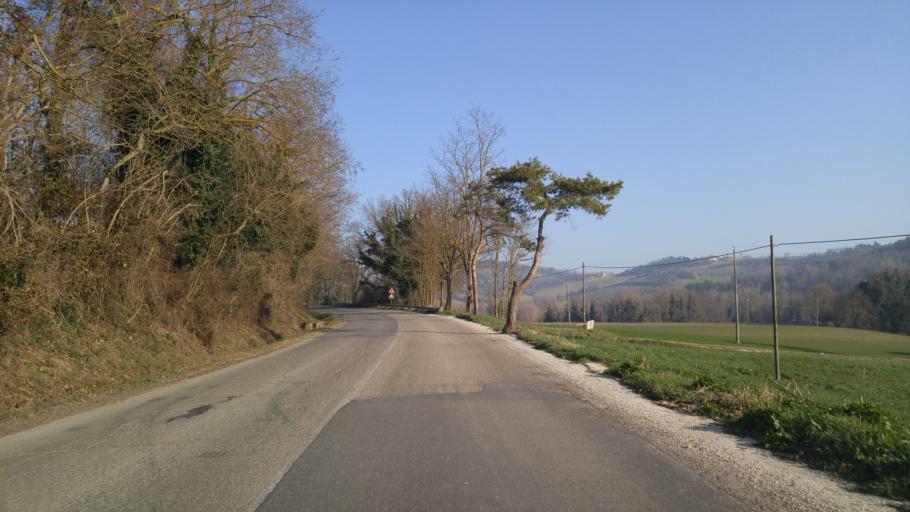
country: IT
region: The Marches
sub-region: Provincia di Pesaro e Urbino
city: Fenile
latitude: 43.8331
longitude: 12.9204
